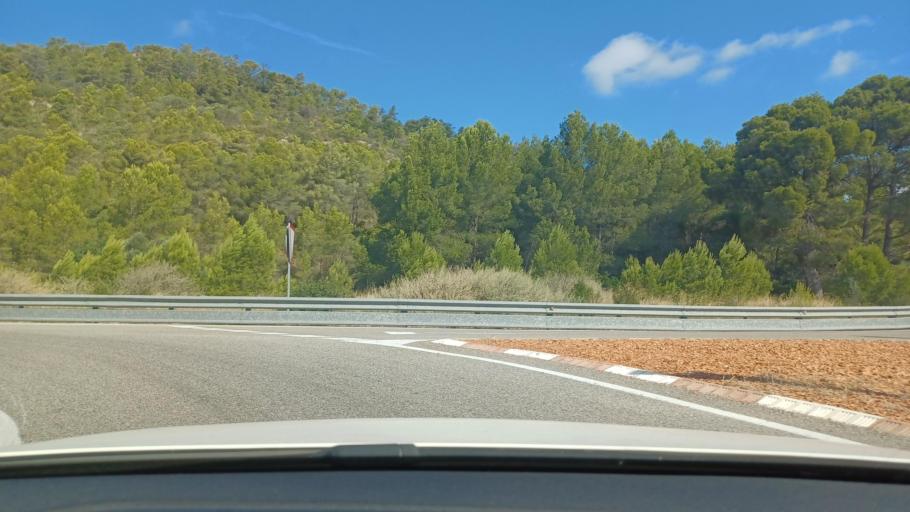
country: ES
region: Catalonia
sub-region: Provincia de Tarragona
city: Bot
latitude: 40.9736
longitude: 0.4458
